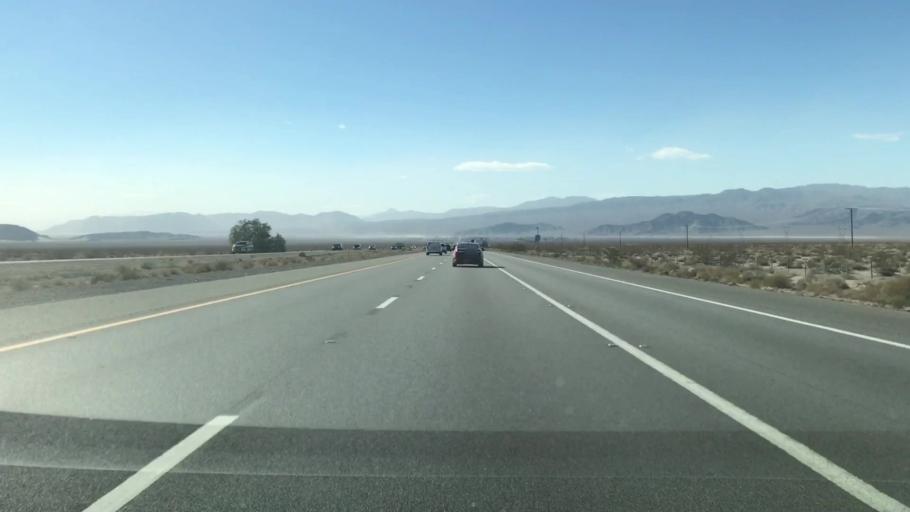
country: US
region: Nevada
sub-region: Clark County
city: Sandy Valley
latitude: 35.3123
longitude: -116.0003
